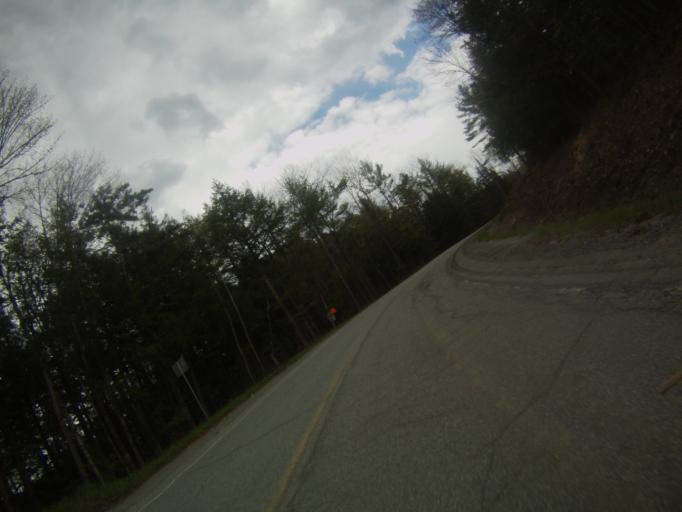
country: US
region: New York
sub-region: Essex County
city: Mineville
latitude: 44.0820
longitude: -73.6117
